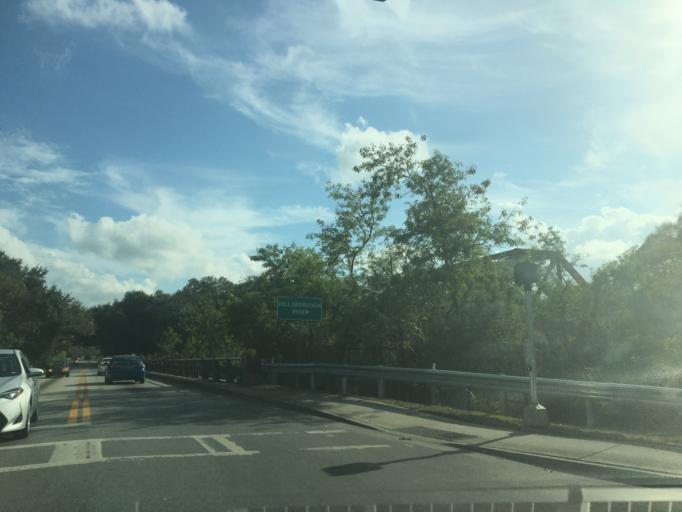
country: US
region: Florida
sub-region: Hillsborough County
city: University
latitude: 28.0225
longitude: -82.4352
